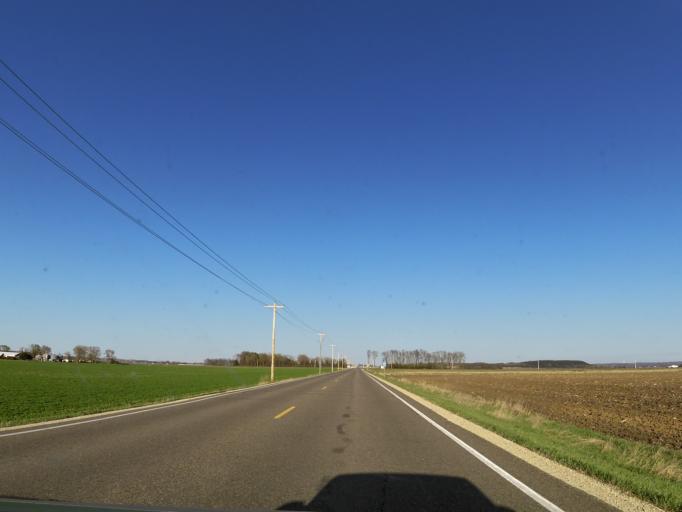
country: US
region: Minnesota
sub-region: Goodhue County
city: Cannon Falls
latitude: 44.5434
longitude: -93.0023
